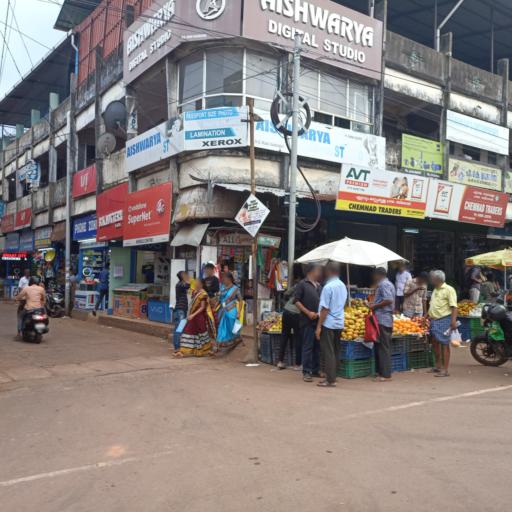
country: IN
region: Kerala
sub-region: Kasaragod District
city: Kasaragod
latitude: 12.5007
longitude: 74.9894
